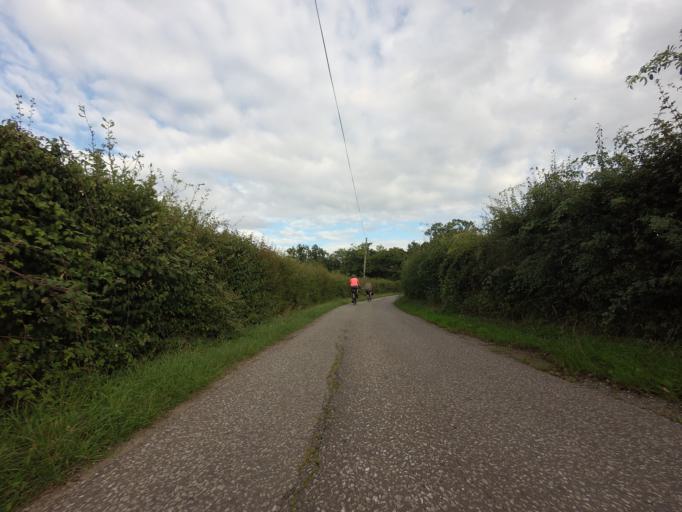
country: GB
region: England
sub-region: Kent
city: Staplehurst
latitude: 51.2105
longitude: 0.5591
